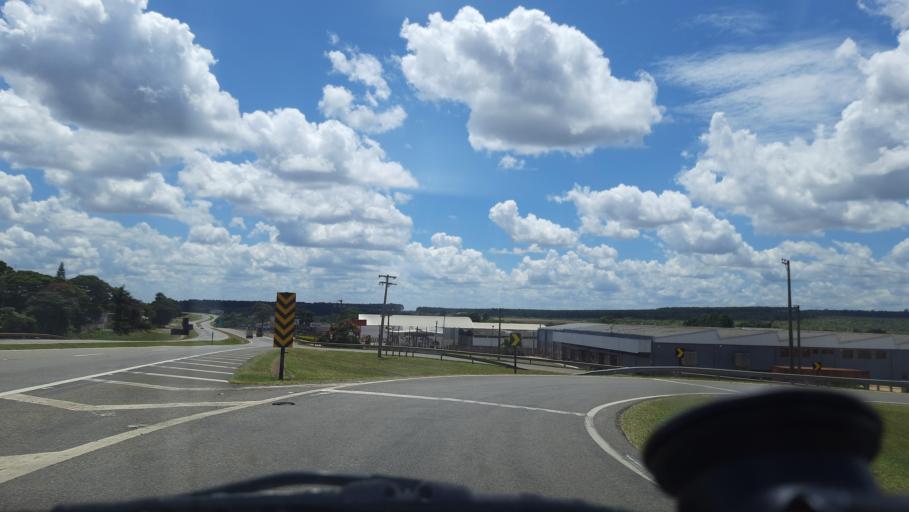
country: BR
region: Sao Paulo
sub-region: Casa Branca
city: Casa Branca
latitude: -21.7851
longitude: -47.0639
